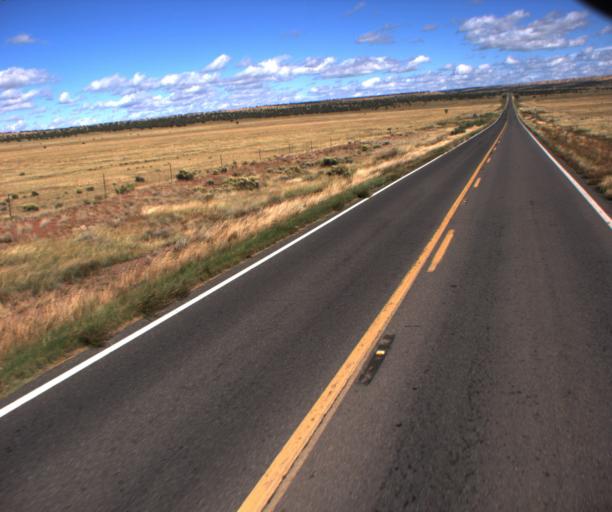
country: US
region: Arizona
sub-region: Apache County
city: Saint Johns
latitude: 34.7583
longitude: -109.2429
